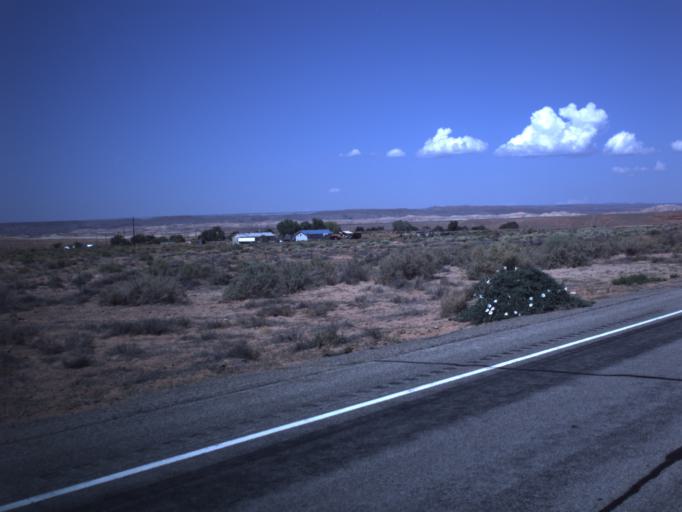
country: US
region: Utah
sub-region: San Juan County
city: Blanding
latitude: 37.2121
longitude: -109.6111
